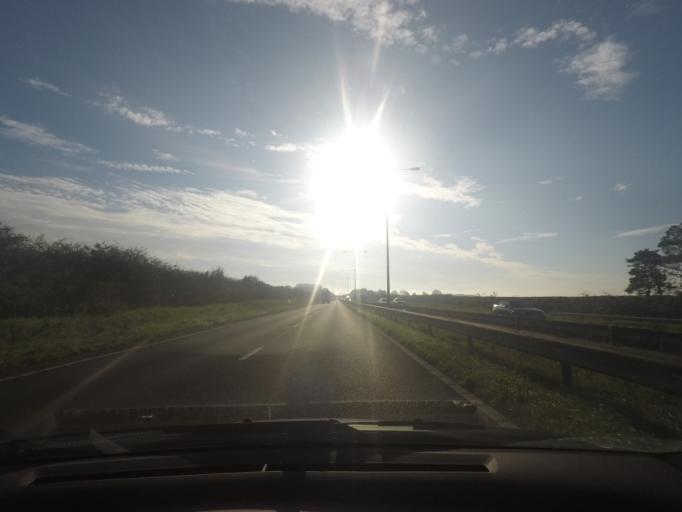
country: GB
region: England
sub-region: East Riding of Yorkshire
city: Brantingham
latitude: 53.7540
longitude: -0.5826
